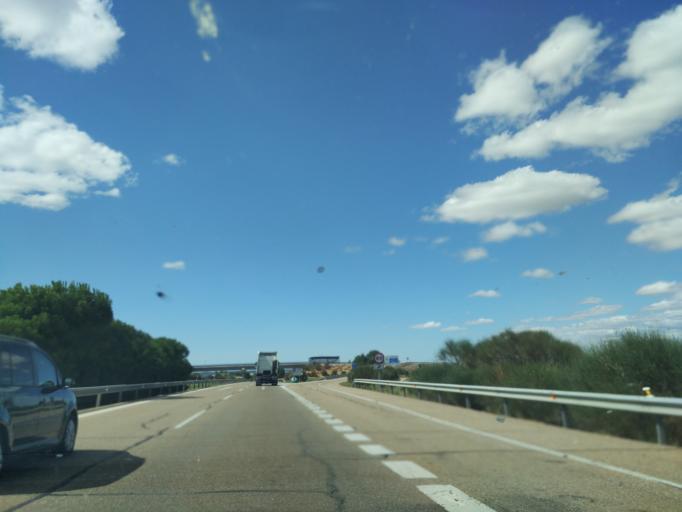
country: ES
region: Castille and Leon
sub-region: Provincia de Valladolid
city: Rueda
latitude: 41.4408
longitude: -4.9755
